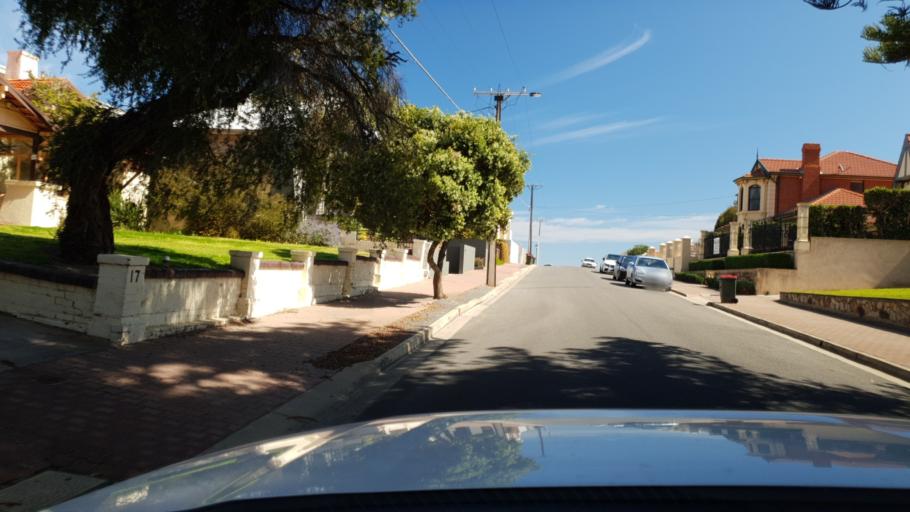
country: AU
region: South Australia
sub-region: Adelaide
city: Glenelg
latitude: -34.9941
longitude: 138.5117
